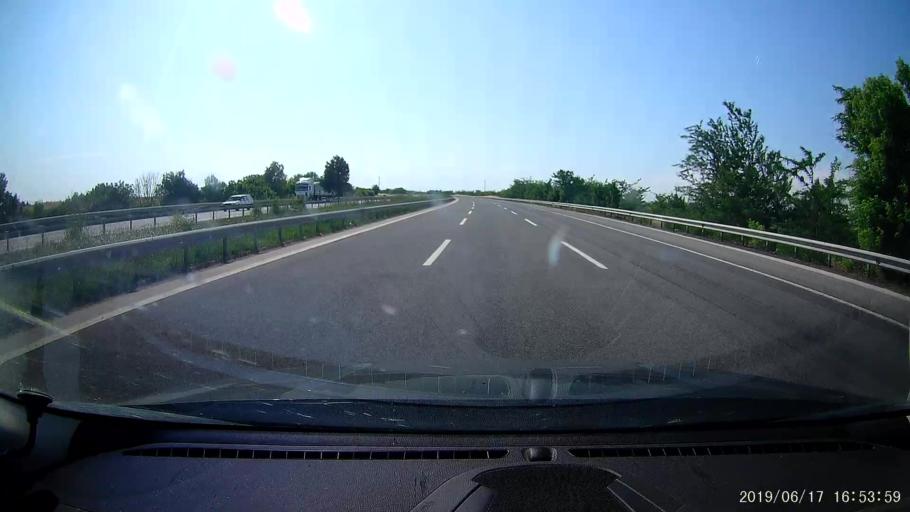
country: TR
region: Kirklareli
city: Inece
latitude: 41.5702
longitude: 27.0094
